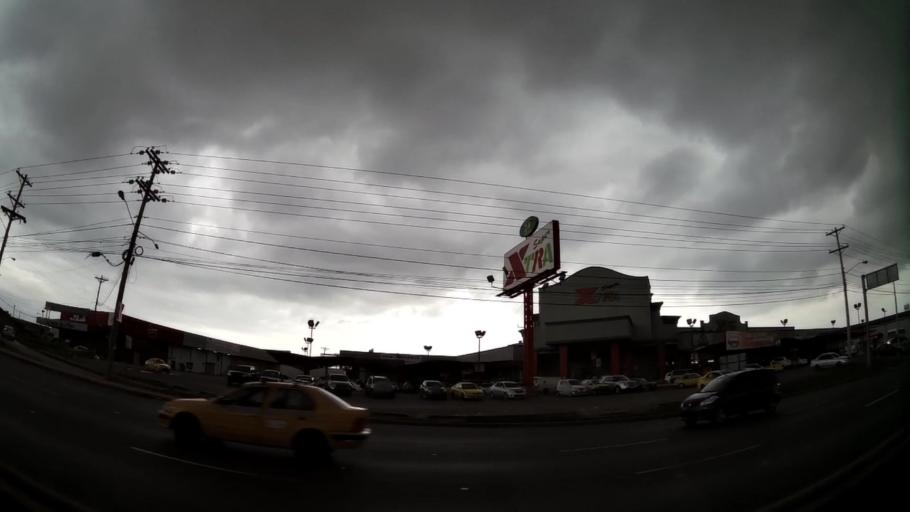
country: PA
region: Panama
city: San Miguelito
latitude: 9.0603
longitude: -79.4277
